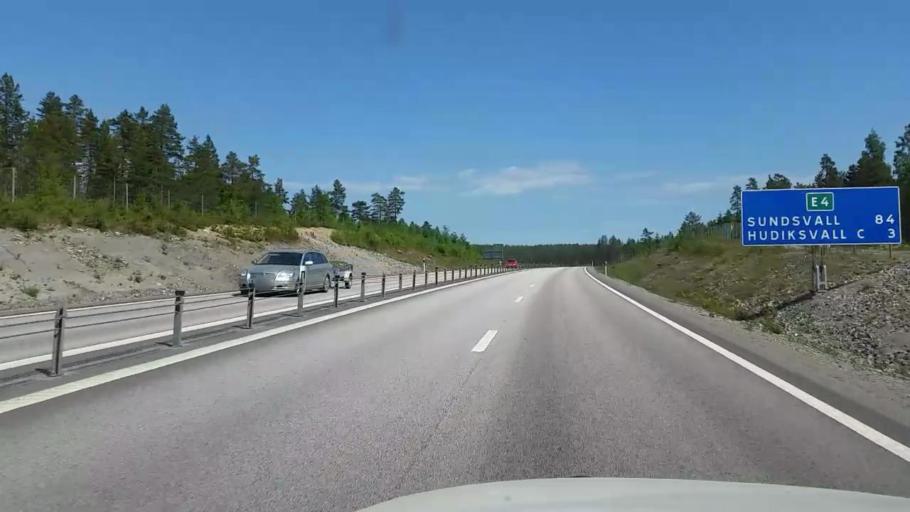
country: SE
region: Gaevleborg
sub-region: Hudiksvalls Kommun
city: Hudiksvall
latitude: 61.7203
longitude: 17.0565
